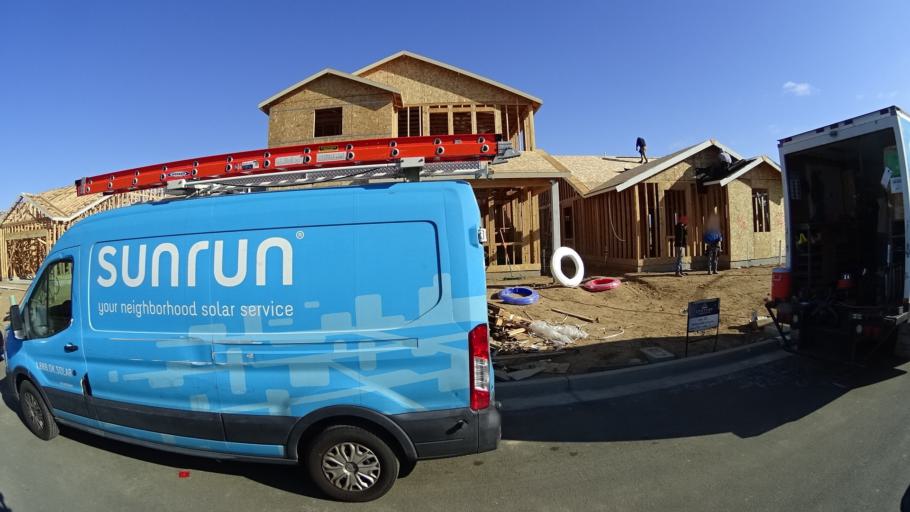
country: US
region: California
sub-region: Fresno County
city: West Park
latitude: 36.8040
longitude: -119.9043
